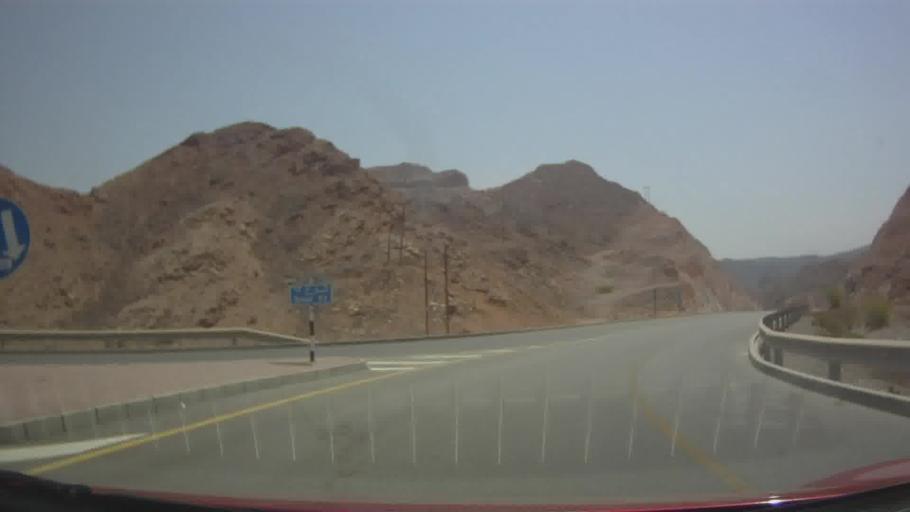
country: OM
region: Muhafazat Masqat
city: Muscat
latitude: 23.5236
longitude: 58.6335
